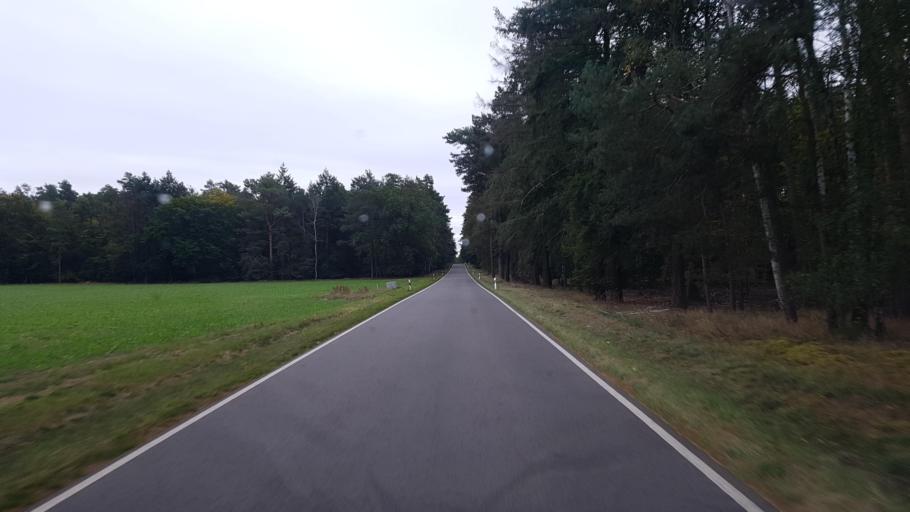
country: DE
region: Brandenburg
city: Luckau
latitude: 51.8866
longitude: 13.6645
